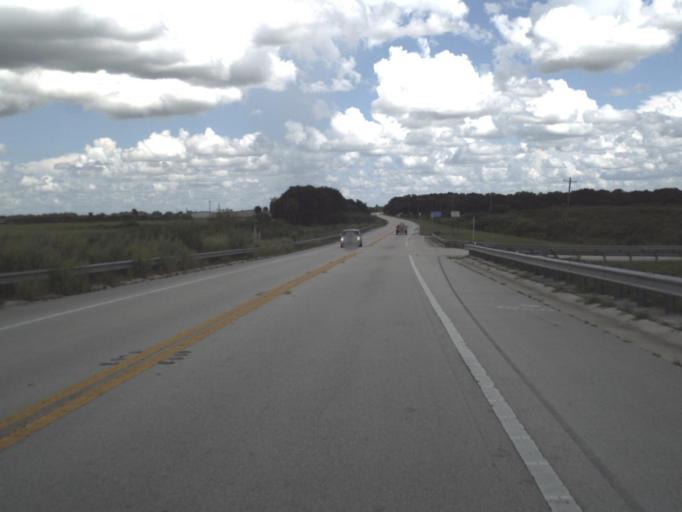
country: US
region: Florida
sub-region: Polk County
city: Babson Park
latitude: 27.8048
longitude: -81.1953
